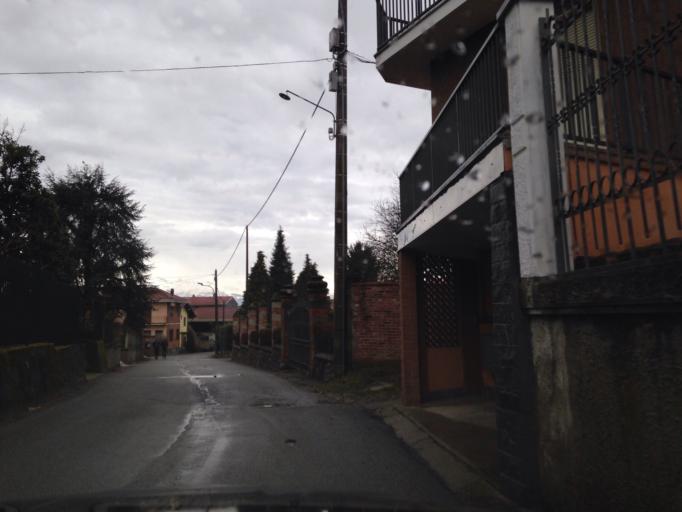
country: IT
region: Piedmont
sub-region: Provincia di Vercelli
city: Moncrivello
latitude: 45.3336
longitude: 7.9955
